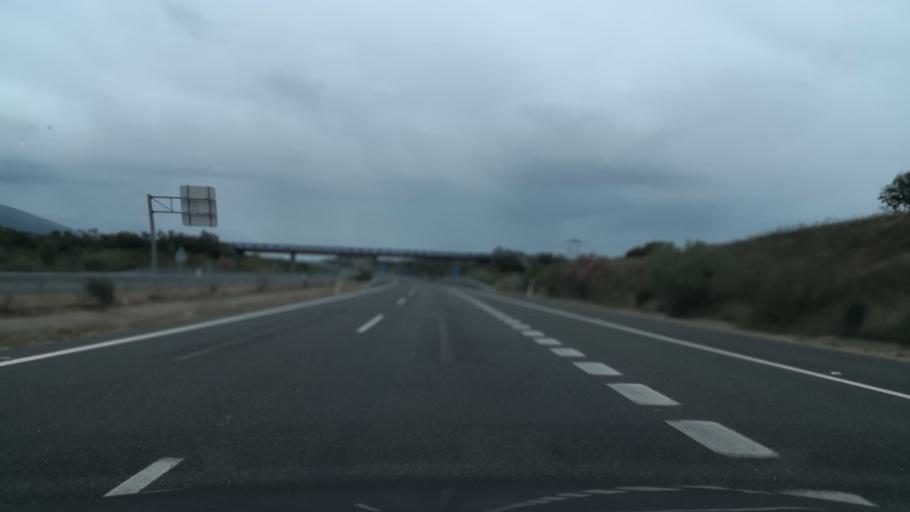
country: ES
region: Extremadura
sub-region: Provincia de Caceres
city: Jarilla
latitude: 40.1867
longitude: -6.0110
